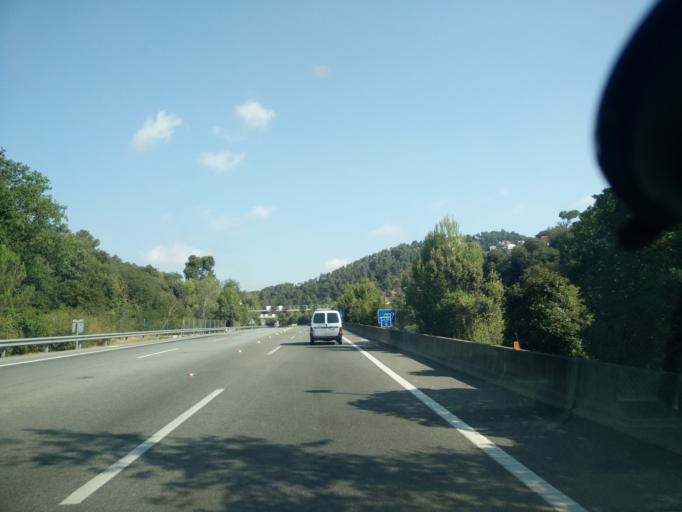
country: ES
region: Catalonia
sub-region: Provincia de Barcelona
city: Sant Just Desvern
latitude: 41.4242
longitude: 2.0930
